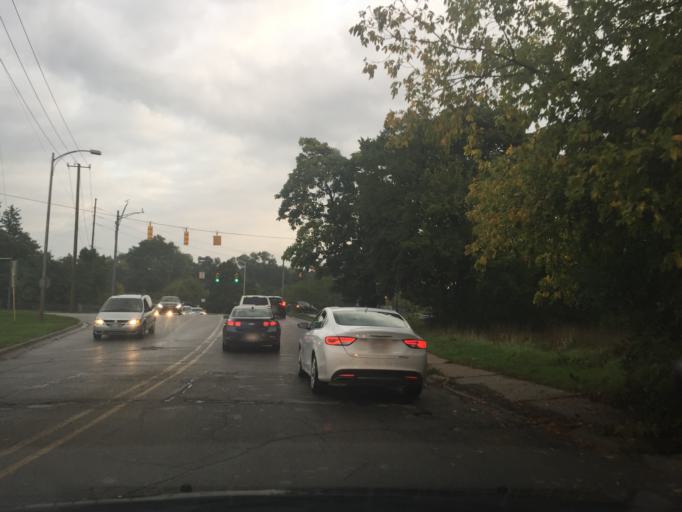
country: US
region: Michigan
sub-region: Oakland County
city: Pontiac
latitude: 42.6402
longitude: -83.2821
